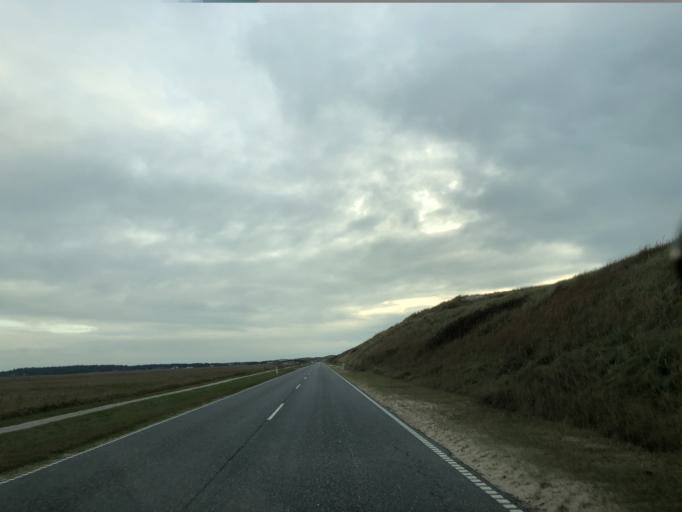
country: DK
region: Central Jutland
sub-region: Holstebro Kommune
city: Ulfborg
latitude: 56.3342
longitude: 8.1230
